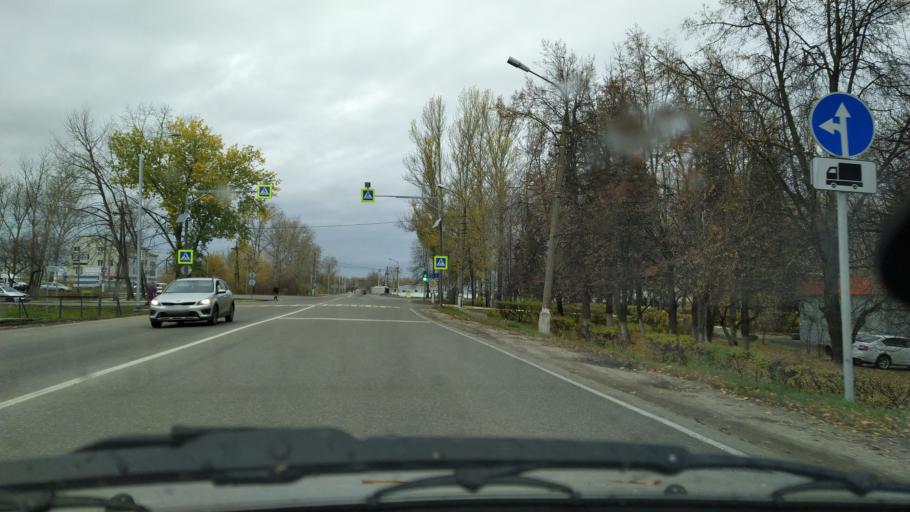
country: RU
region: Moskovskaya
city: Voskresensk
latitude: 55.3163
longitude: 38.6492
